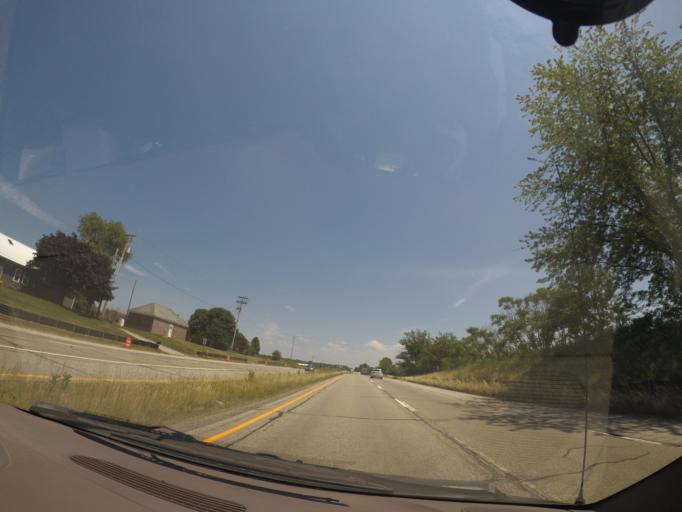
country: US
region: Indiana
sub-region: LaPorte County
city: Hudson Lake
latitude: 41.6726
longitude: -86.5645
